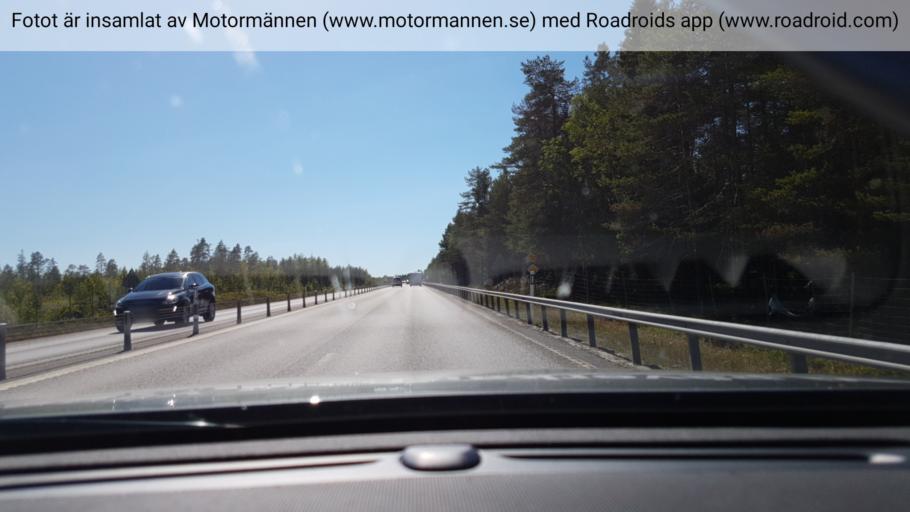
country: SE
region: Vaesterbotten
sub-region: Robertsfors Kommun
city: Robertsfors
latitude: 63.9927
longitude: 20.7628
